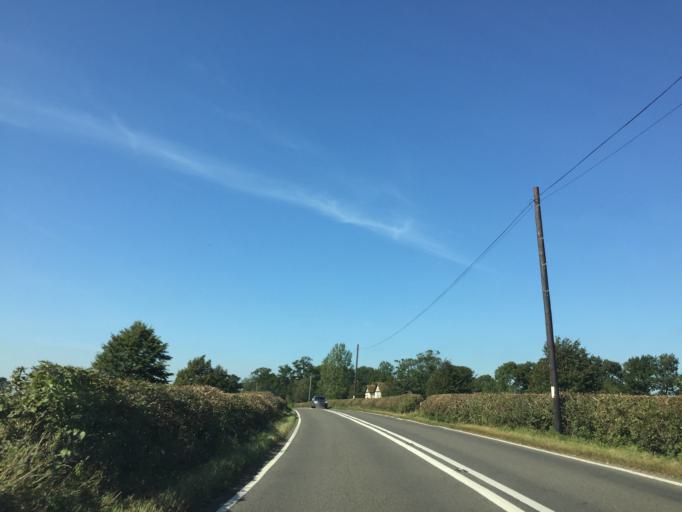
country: GB
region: England
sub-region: Leicestershire
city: Houghton on the Hill
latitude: 52.6730
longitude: -0.9349
